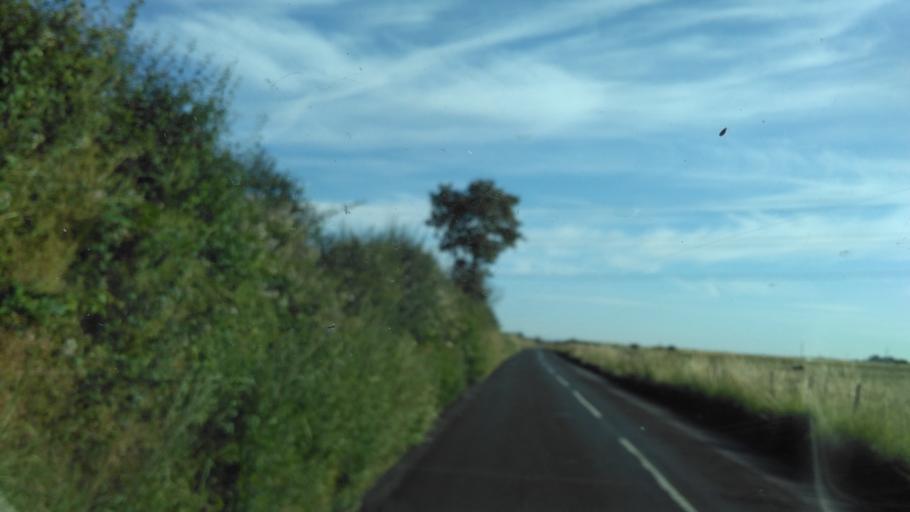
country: GB
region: England
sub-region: Kent
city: Dunkirk
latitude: 51.3354
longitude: 0.9519
